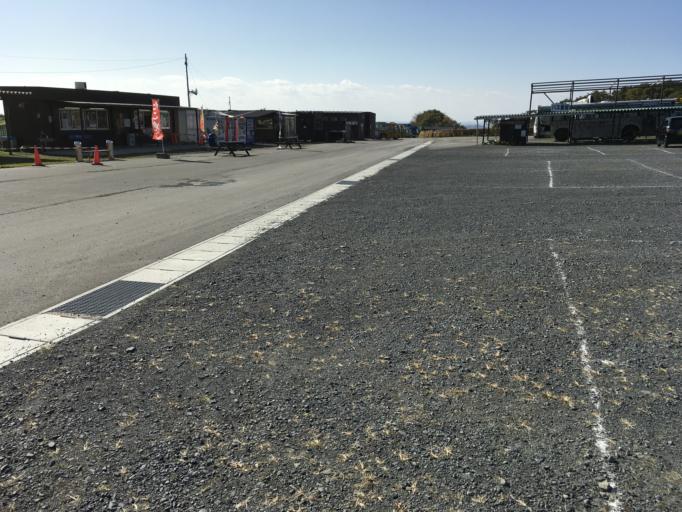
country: JP
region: Iwate
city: Ichinoseki
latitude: 38.8089
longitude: 141.2596
